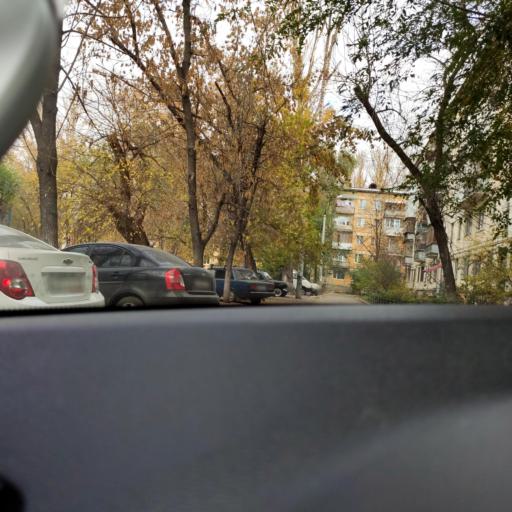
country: RU
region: Samara
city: Samara
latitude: 53.2097
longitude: 50.1660
